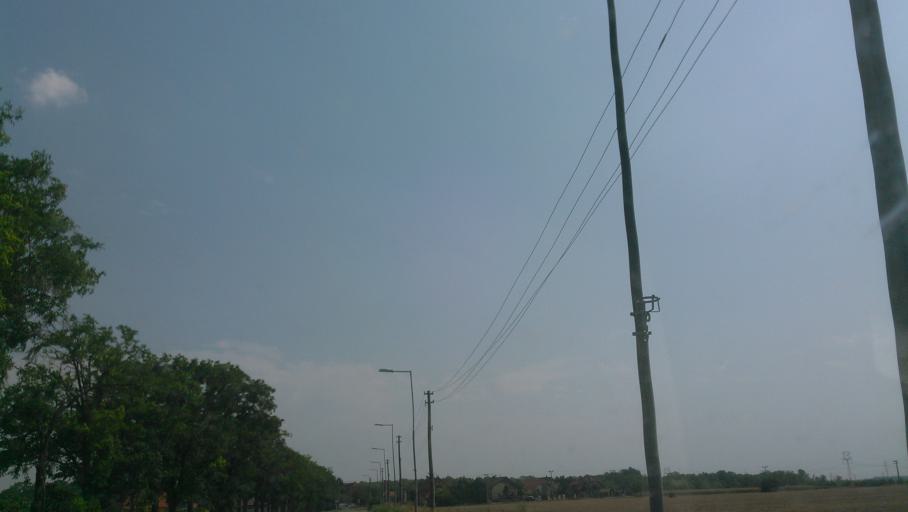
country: SK
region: Trnavsky
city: Samorin
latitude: 48.0546
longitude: 17.4467
